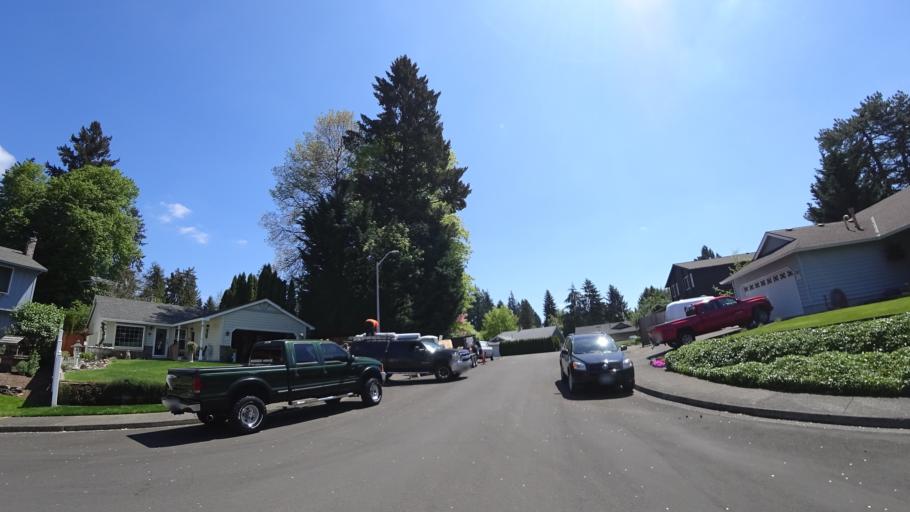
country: US
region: Oregon
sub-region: Washington County
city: Hillsboro
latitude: 45.5142
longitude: -122.9808
